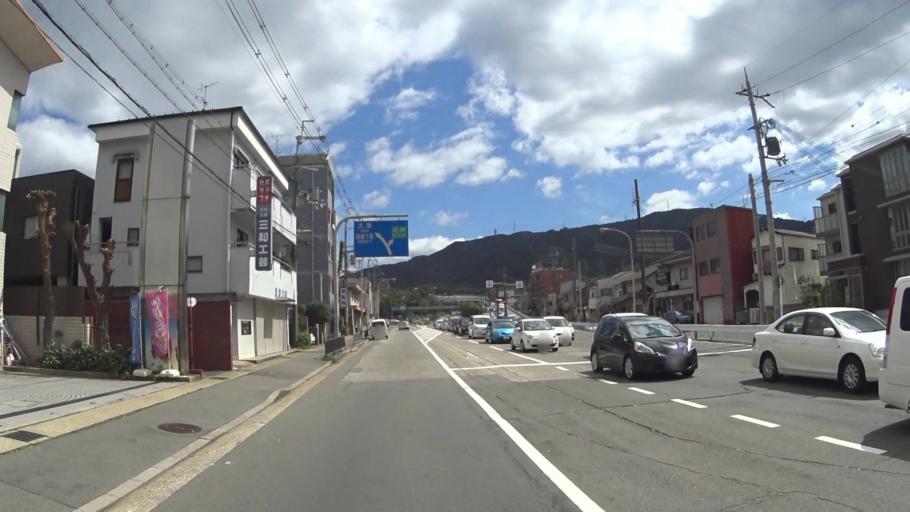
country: JP
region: Shiga Prefecture
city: Otsu-shi
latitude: 34.9897
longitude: 135.8243
